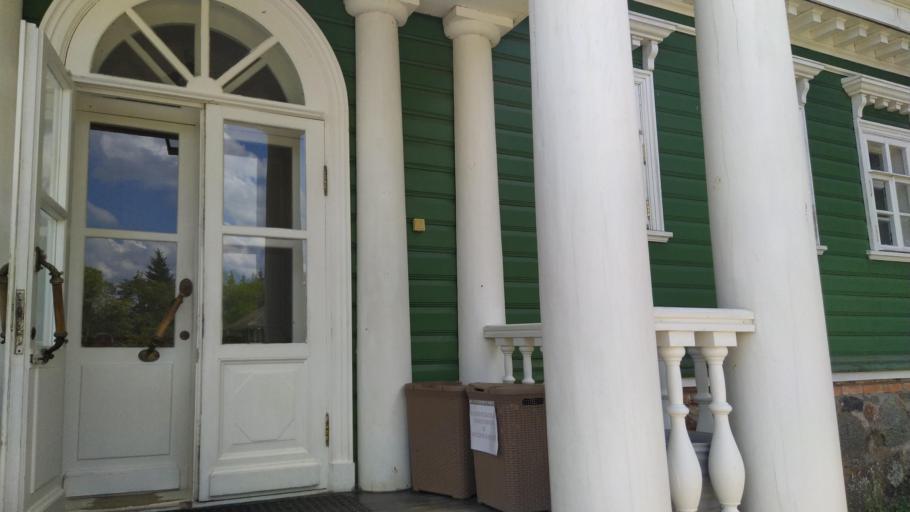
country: RU
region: Pskov
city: Pushkinskiye Gory
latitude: 57.0789
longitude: 28.9499
